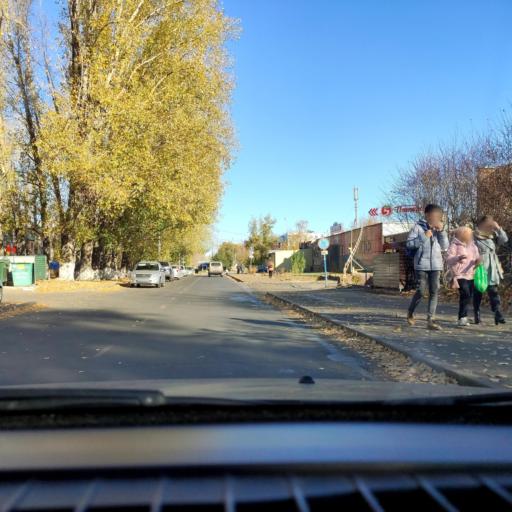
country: RU
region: Samara
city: Tol'yatti
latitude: 53.5265
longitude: 49.2912
